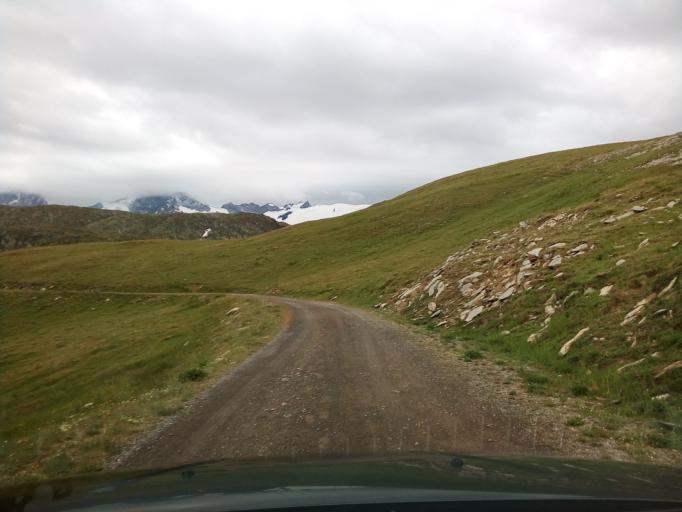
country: FR
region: Rhone-Alpes
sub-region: Departement de l'Isere
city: Mont-de-Lans
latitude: 45.0649
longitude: 6.2138
